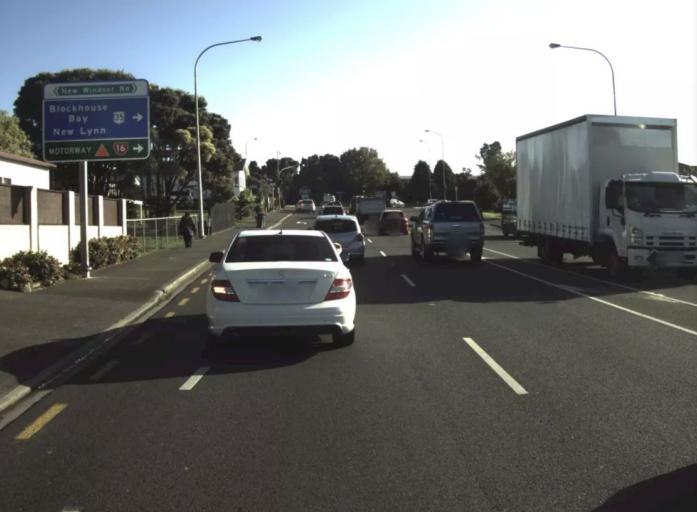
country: NZ
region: Auckland
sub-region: Auckland
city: Rosebank
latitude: -36.9069
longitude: 174.7150
